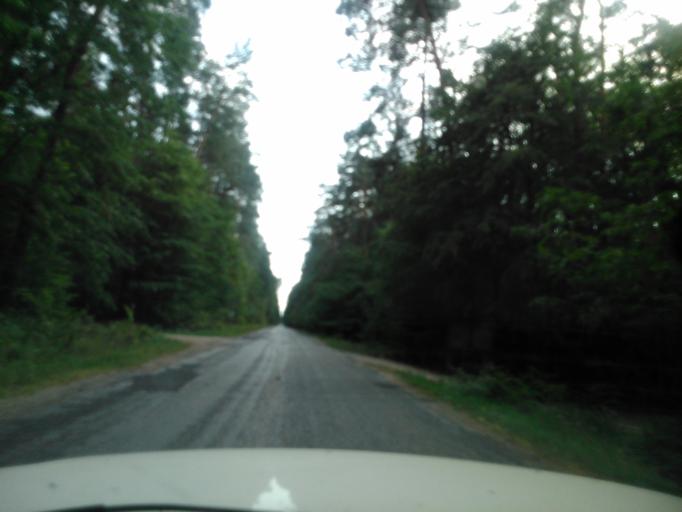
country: PL
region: Kujawsko-Pomorskie
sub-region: Powiat wabrzeski
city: Debowa Laka
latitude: 53.1900
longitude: 19.1529
